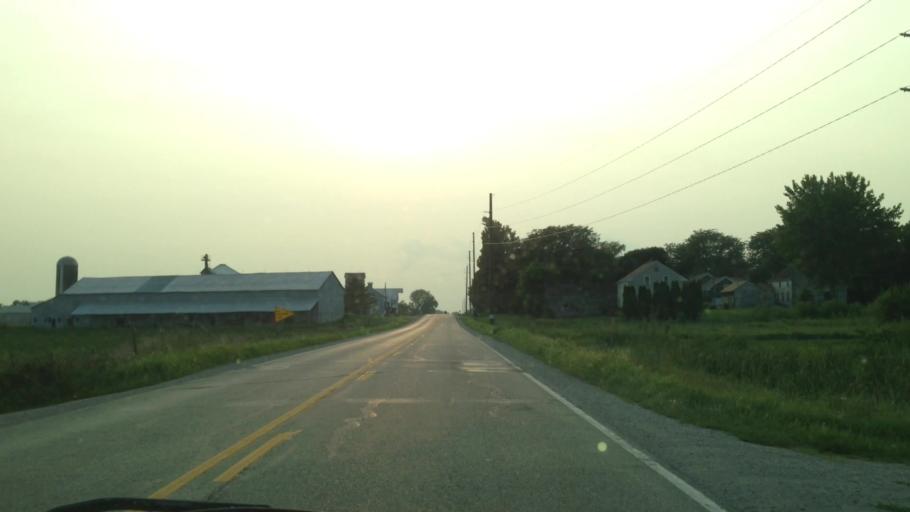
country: US
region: Iowa
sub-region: Benton County
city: Walford
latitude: 41.8020
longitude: -91.9383
